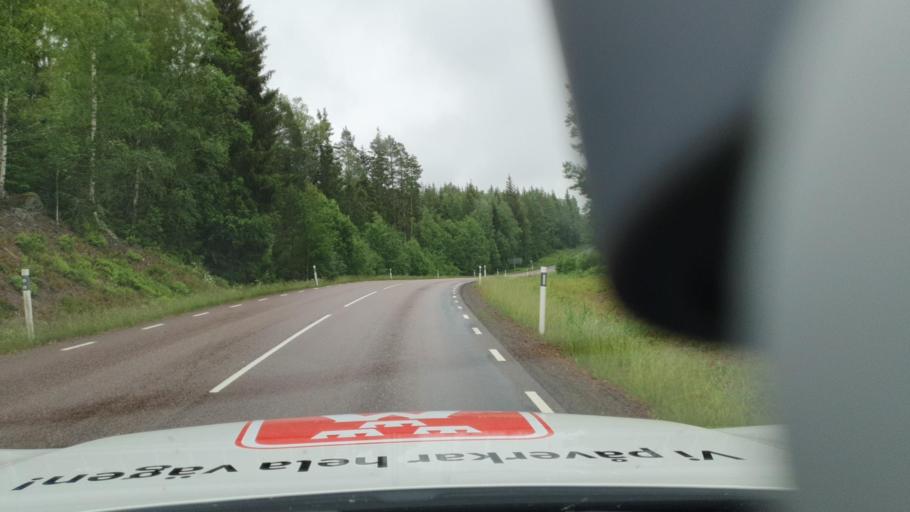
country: SE
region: Vaermland
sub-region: Kristinehamns Kommun
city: Bjorneborg
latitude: 59.2356
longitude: 14.2917
